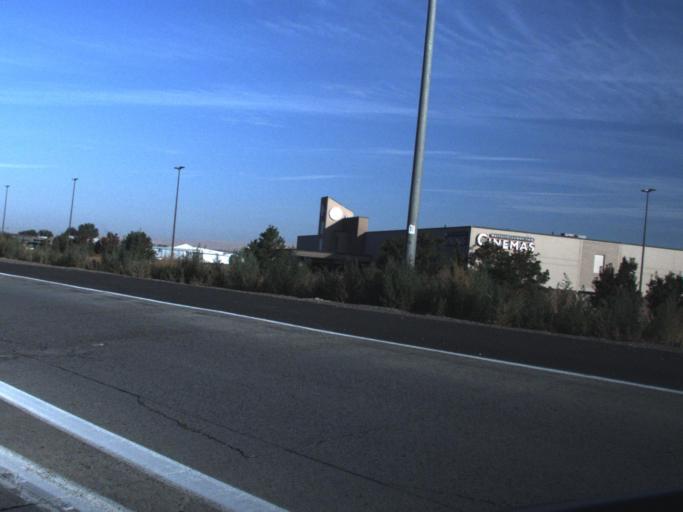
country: US
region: Washington
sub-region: Yakima County
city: Sunnyside
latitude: 46.3062
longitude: -119.9729
